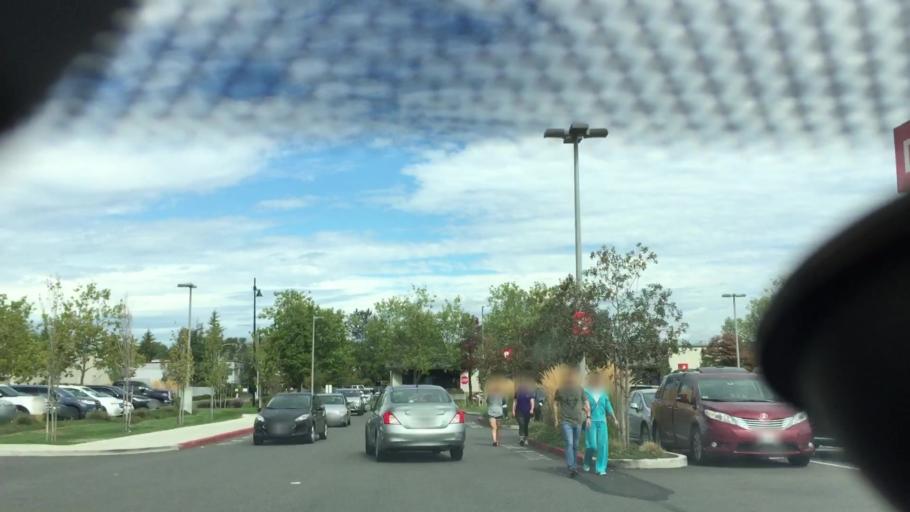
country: US
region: Washington
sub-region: King County
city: Renton
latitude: 47.4431
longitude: -122.2273
